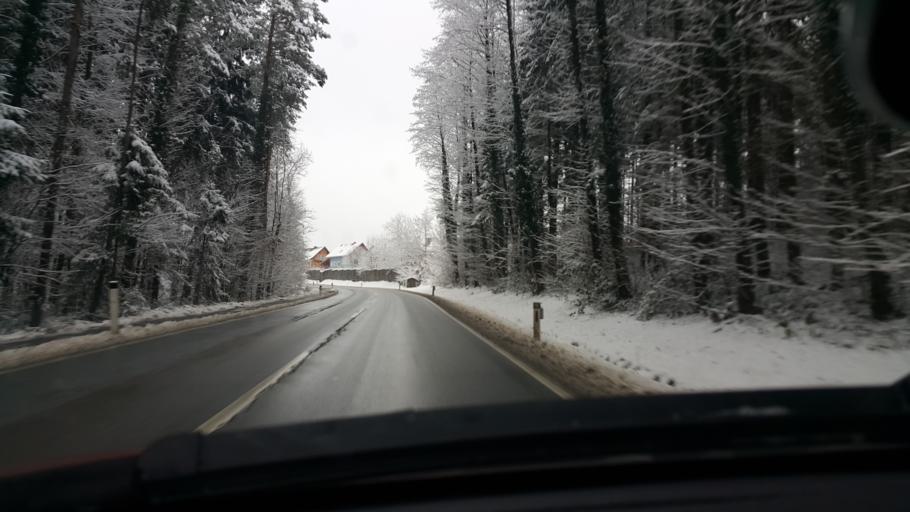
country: AT
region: Styria
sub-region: Politischer Bezirk Graz-Umgebung
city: Hitzendorf
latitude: 47.0221
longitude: 15.2917
